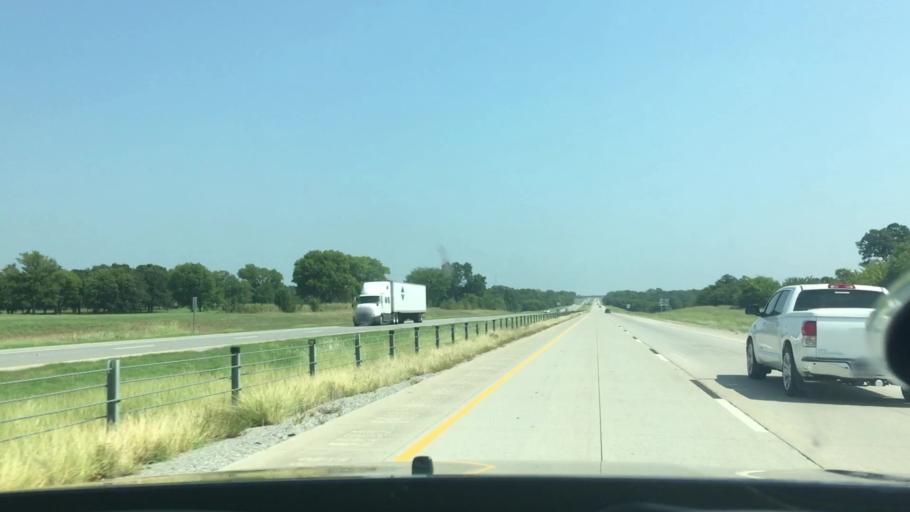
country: US
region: Oklahoma
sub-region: Bryan County
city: Durant
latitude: 34.0547
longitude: -96.3548
